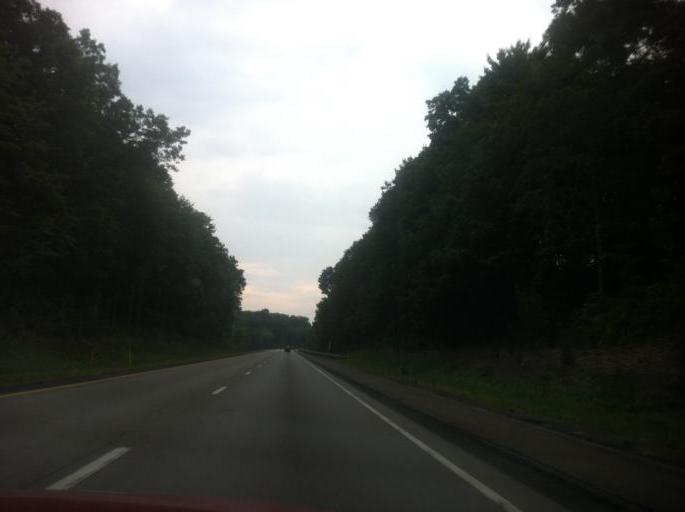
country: US
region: Pennsylvania
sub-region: Clarion County
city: Clarion
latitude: 41.1760
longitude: -79.2595
